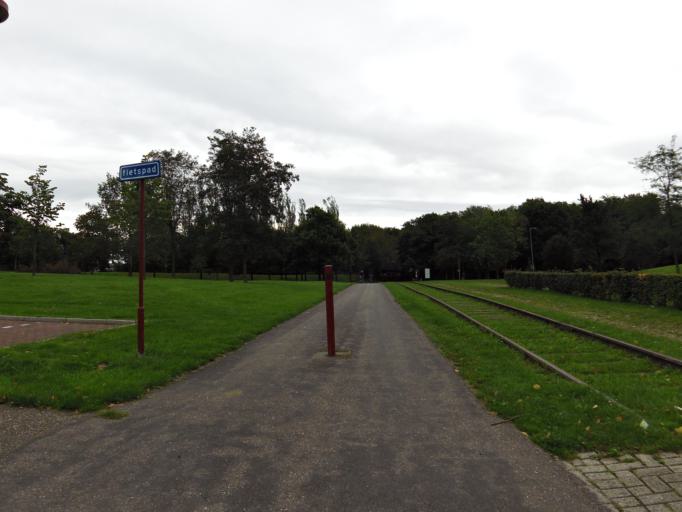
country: NL
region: Limburg
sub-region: Gemeente Heerlen
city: Heerlen
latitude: 50.8724
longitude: 6.0213
